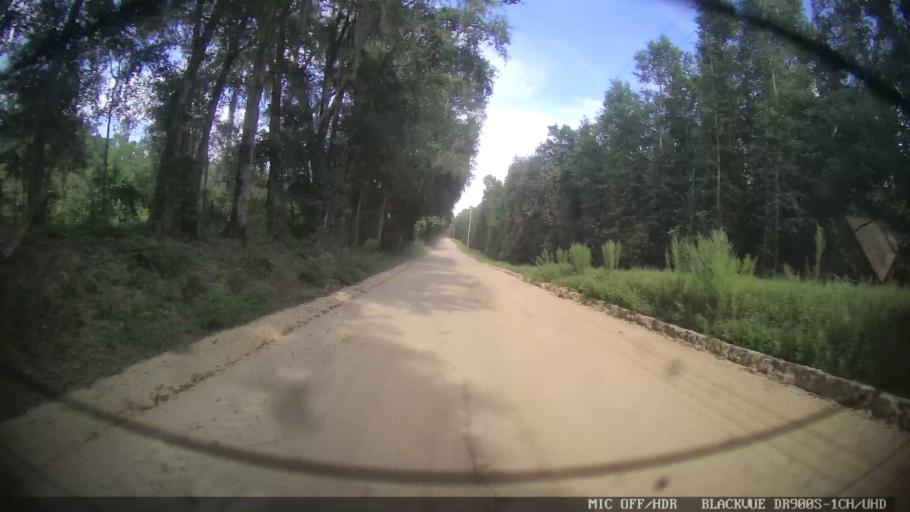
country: US
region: Georgia
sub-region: Lowndes County
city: Valdosta
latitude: 30.6205
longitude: -83.2505
